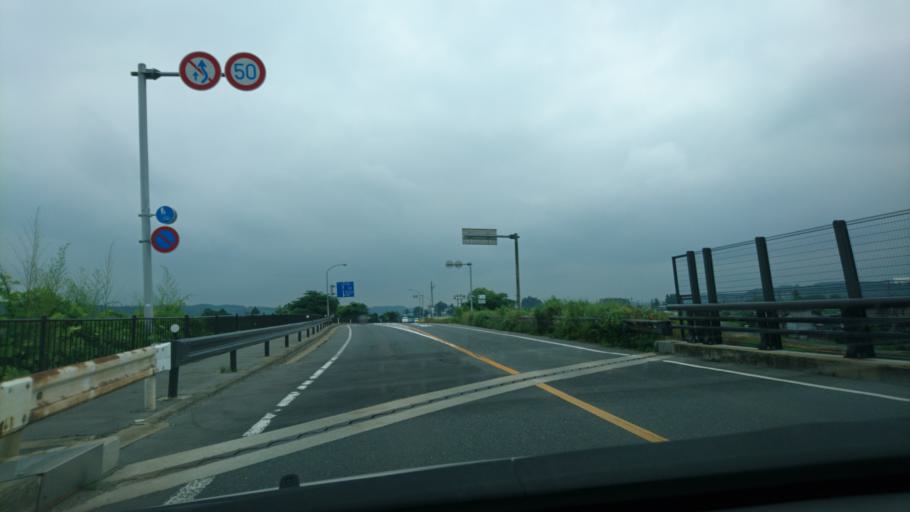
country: JP
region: Miyagi
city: Furukawa
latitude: 38.6779
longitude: 140.8601
